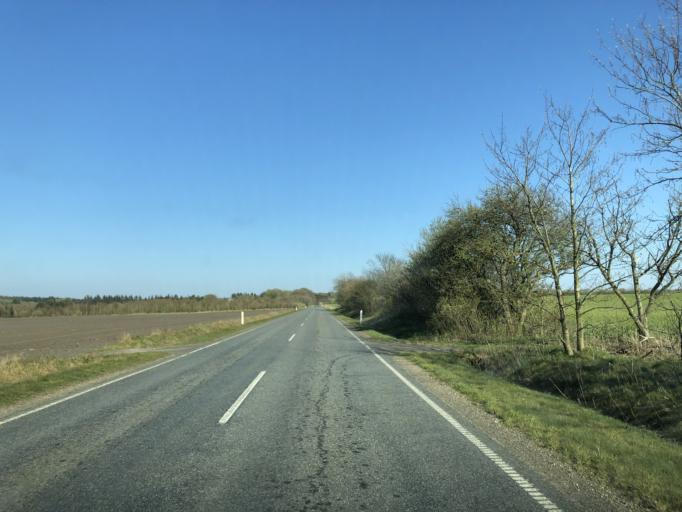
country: DK
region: Central Jutland
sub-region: Holstebro Kommune
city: Ulfborg
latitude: 56.1985
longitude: 8.3989
